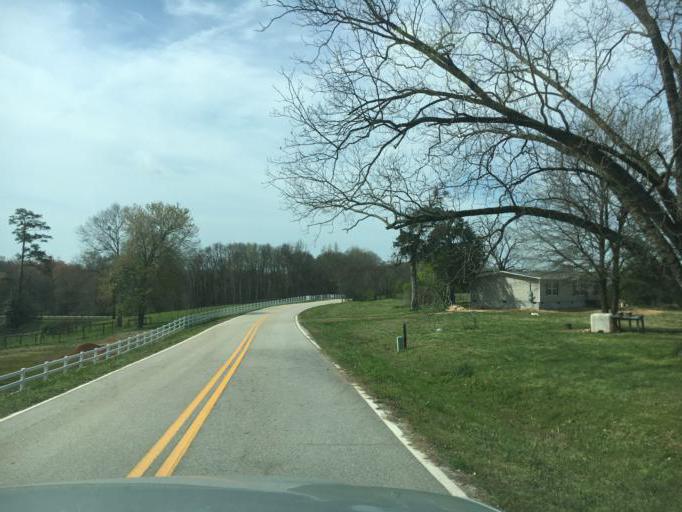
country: US
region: Georgia
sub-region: Franklin County
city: Lavonia
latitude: 34.4373
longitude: -83.0385
